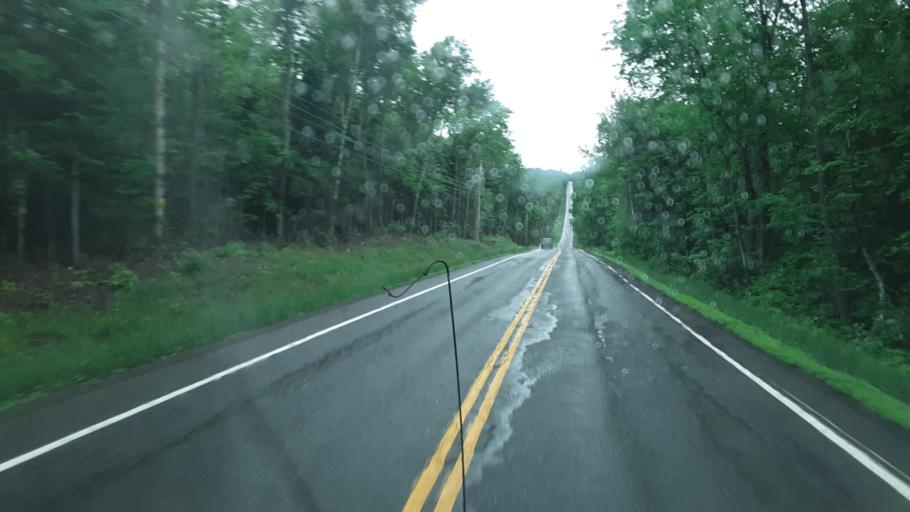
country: US
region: Maine
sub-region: Penobscot County
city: Patten
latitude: 46.1421
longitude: -68.3692
